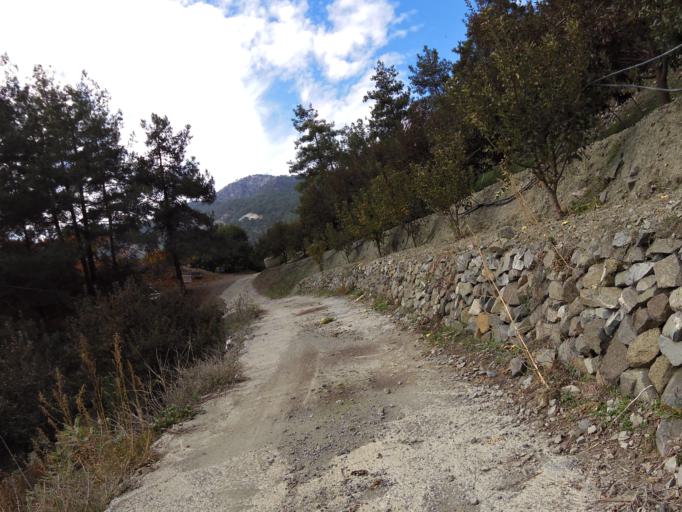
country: CY
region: Limassol
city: Kyperounta
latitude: 34.9325
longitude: 32.9386
